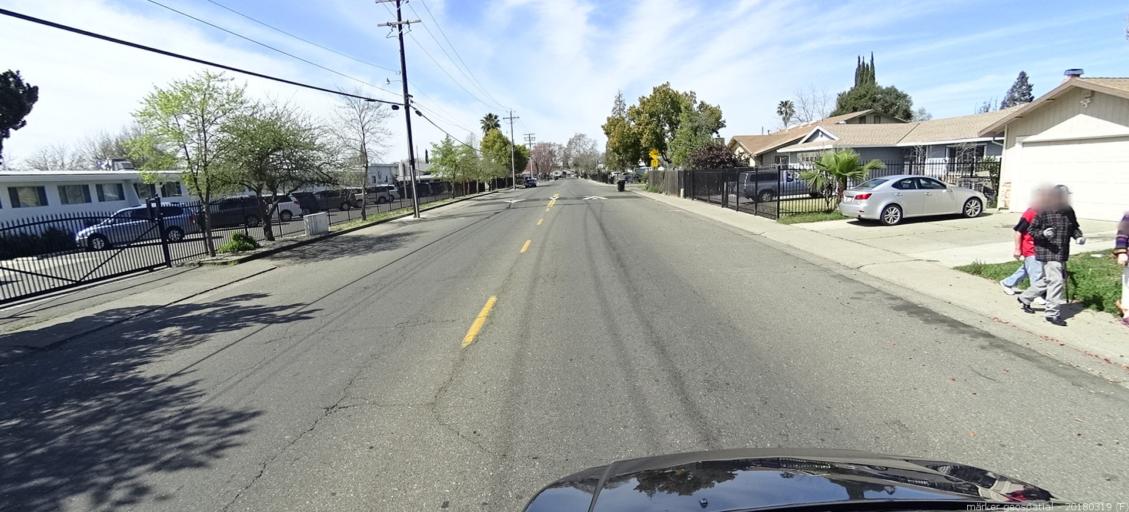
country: US
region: California
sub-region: Sacramento County
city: Parkway
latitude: 38.5158
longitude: -121.4468
